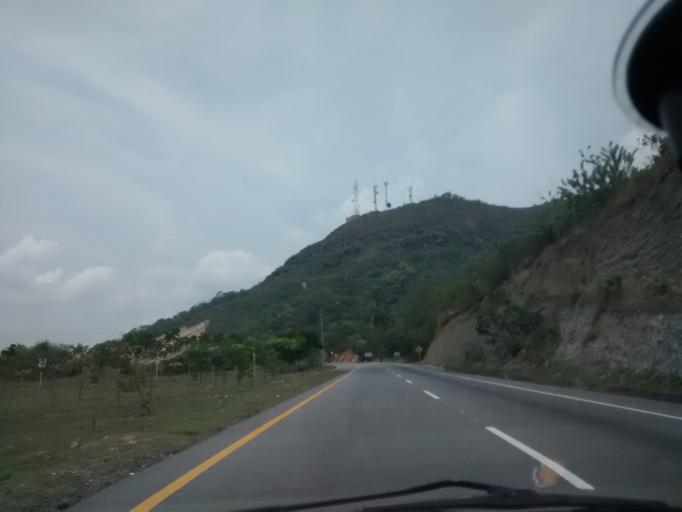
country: CO
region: Tolima
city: Espinal
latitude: 4.2204
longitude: -74.9680
